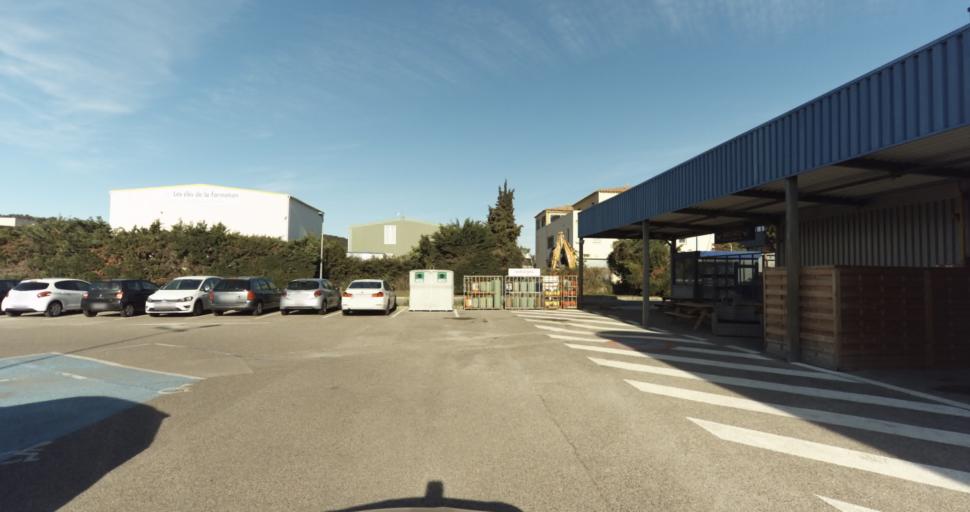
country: FR
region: Provence-Alpes-Cote d'Azur
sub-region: Departement du Var
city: Ollioules
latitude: 43.1182
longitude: 5.8434
